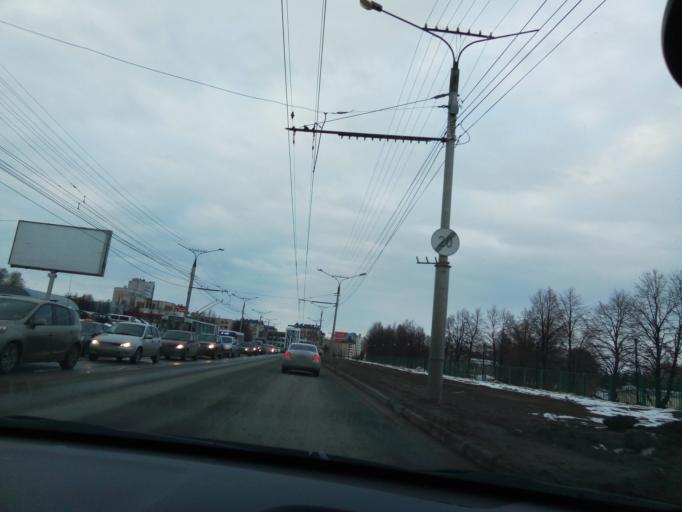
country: RU
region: Chuvashia
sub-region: Cheboksarskiy Rayon
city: Cheboksary
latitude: 56.1453
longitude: 47.2045
